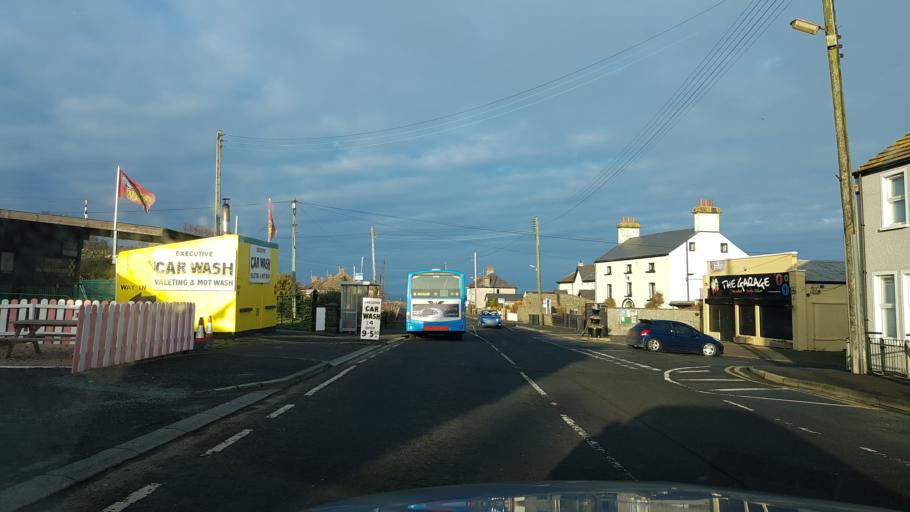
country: GB
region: Northern Ireland
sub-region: Down District
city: Millisle
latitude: 54.6087
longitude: -5.5290
